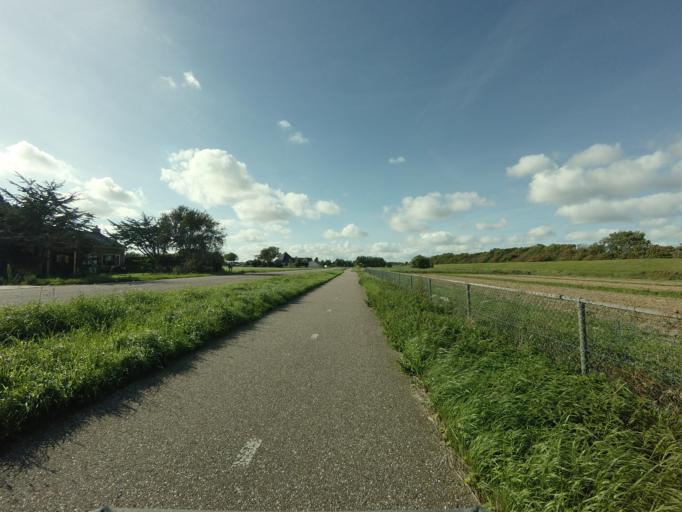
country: NL
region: North Holland
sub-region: Gemeente Den Helder
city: Den Helder
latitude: 52.9082
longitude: 4.8086
